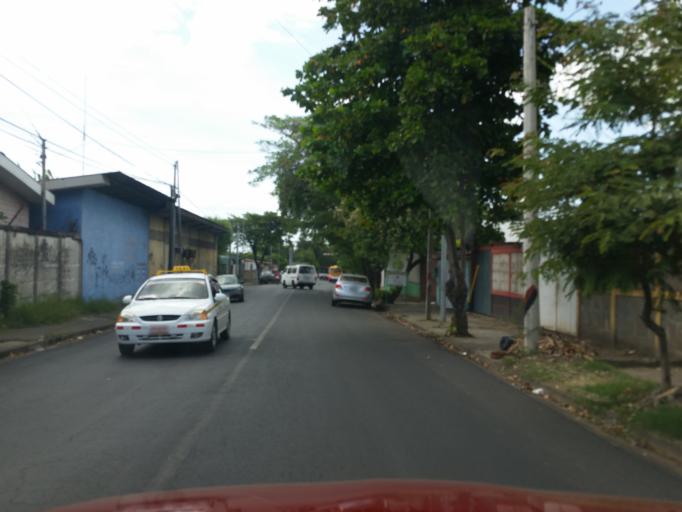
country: NI
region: Managua
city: Managua
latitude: 12.1425
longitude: -86.2651
